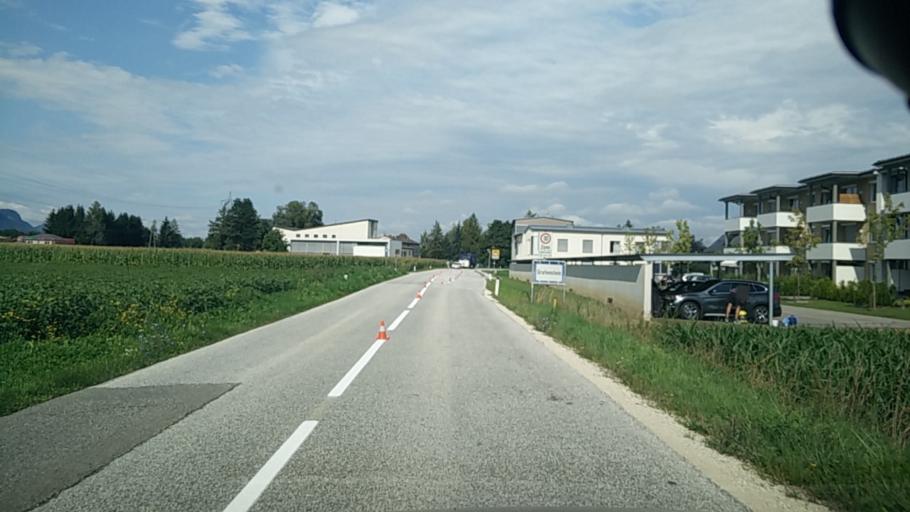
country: AT
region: Carinthia
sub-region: Politischer Bezirk Klagenfurt Land
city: Grafenstein
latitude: 46.6155
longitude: 14.4712
